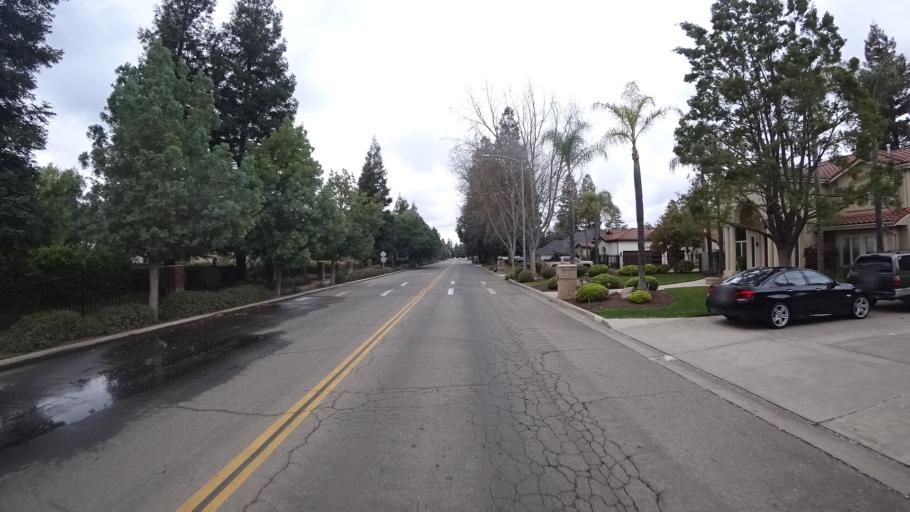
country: US
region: California
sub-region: Fresno County
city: Fresno
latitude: 36.8444
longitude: -119.8433
